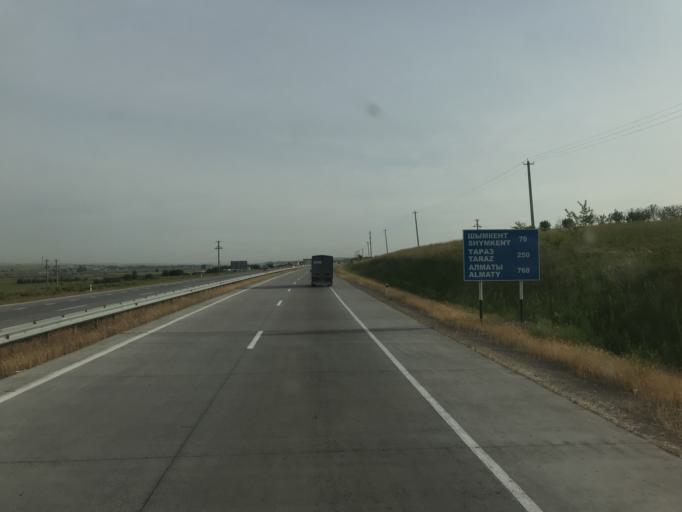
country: KZ
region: Ongtustik Qazaqstan
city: Qazyqurt
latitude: 41.6930
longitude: 69.3949
